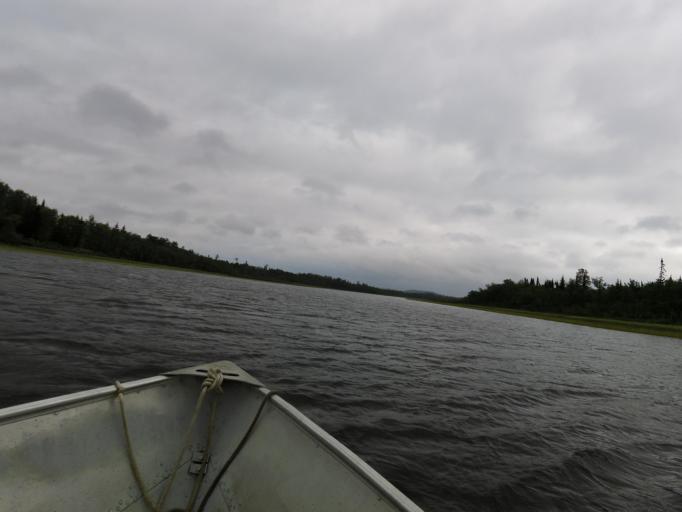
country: CA
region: Ontario
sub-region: Rainy River District
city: Atikokan
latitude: 49.5960
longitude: -91.3561
